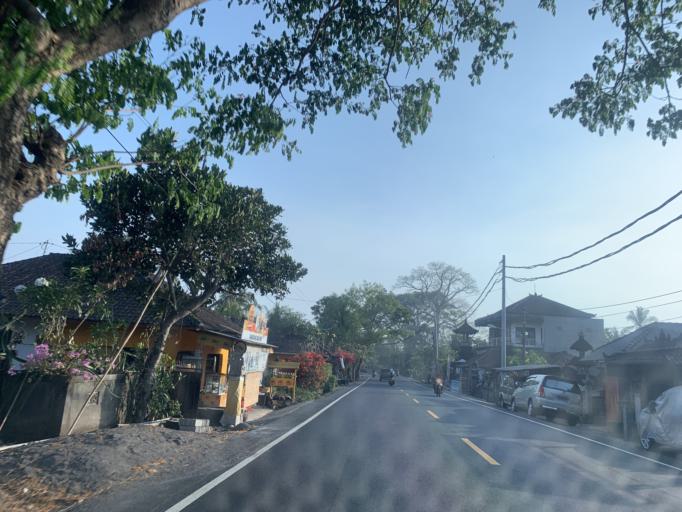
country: ID
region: Bali
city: Banjar Delodrurung
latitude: -8.4996
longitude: 115.0188
